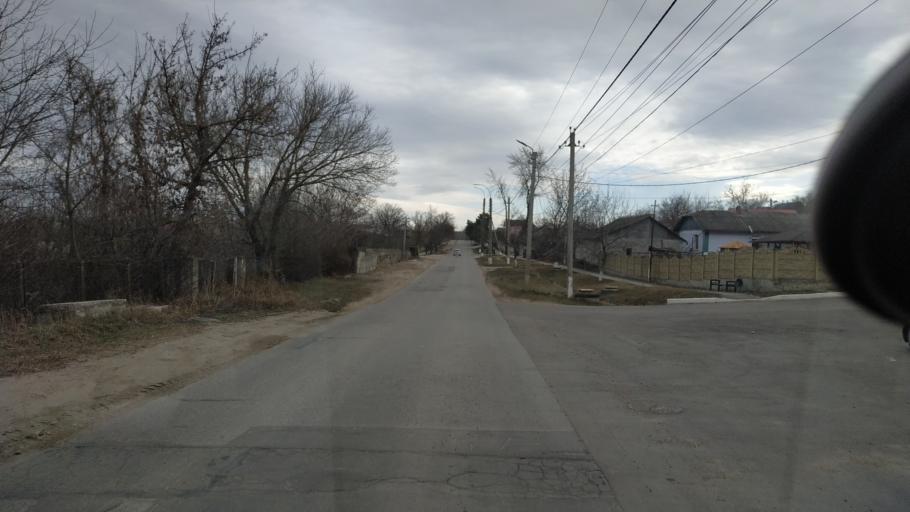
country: MD
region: Chisinau
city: Vadul lui Voda
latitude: 47.0976
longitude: 29.0702
